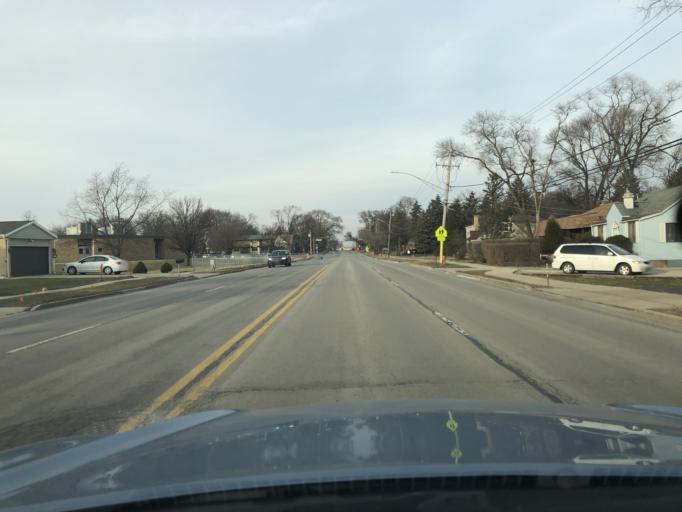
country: US
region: Illinois
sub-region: DuPage County
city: Wood Dale
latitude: 41.9585
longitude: -87.9896
